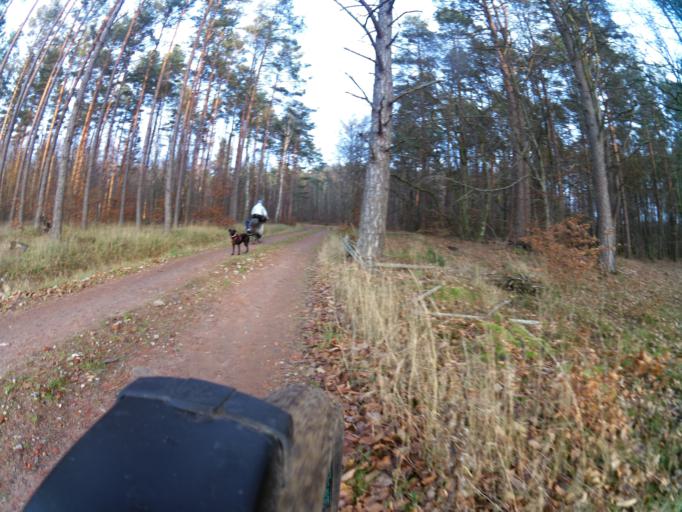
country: PL
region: West Pomeranian Voivodeship
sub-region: Powiat koszalinski
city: Polanow
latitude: 54.1442
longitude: 16.6992
